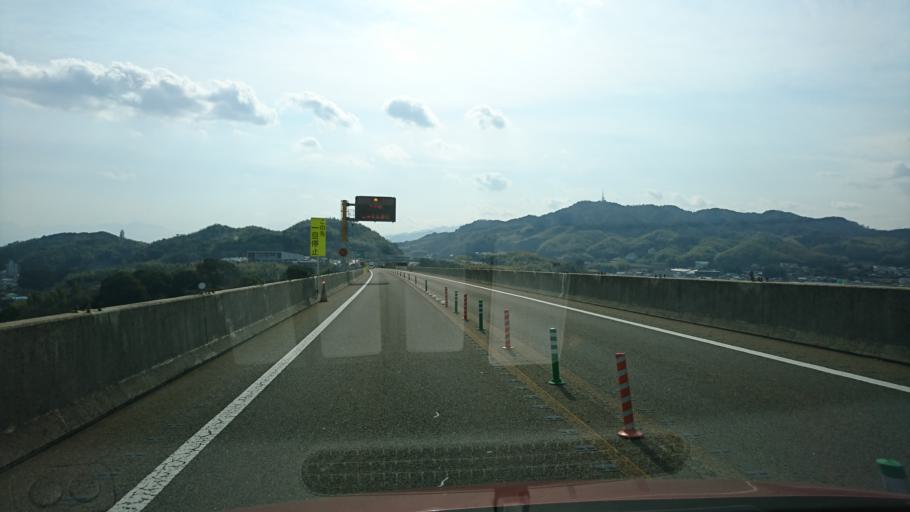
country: JP
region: Ehime
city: Hojo
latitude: 34.1054
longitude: 132.9766
